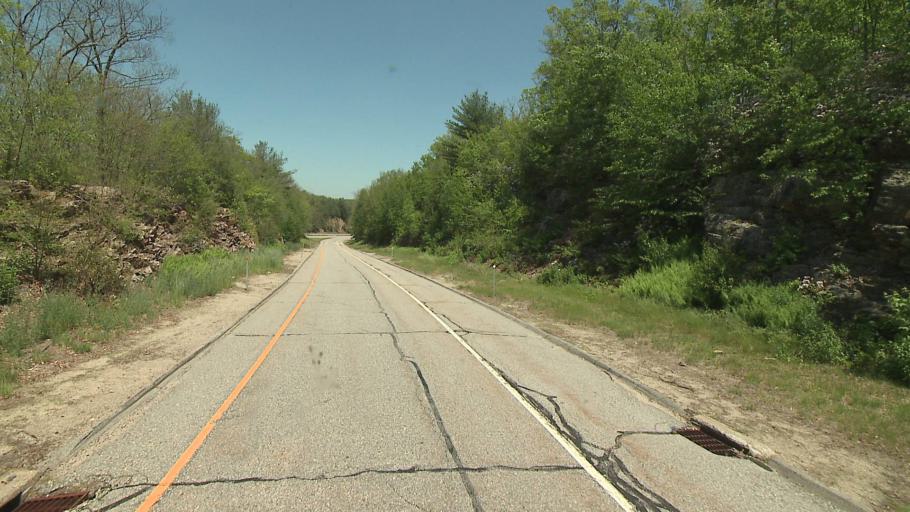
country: US
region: Connecticut
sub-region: Windham County
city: Danielson
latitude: 41.7664
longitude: -71.8684
